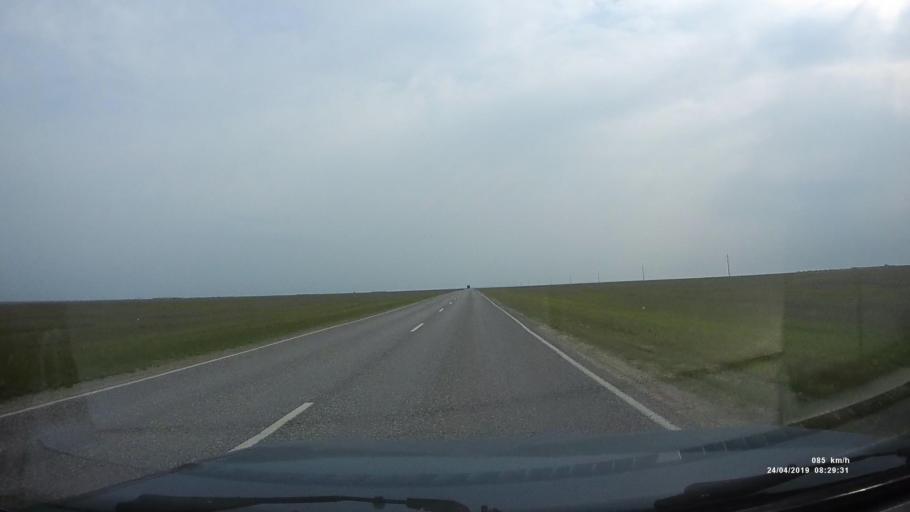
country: RU
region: Kalmykiya
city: Priyutnoye
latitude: 46.1526
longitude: 43.8318
